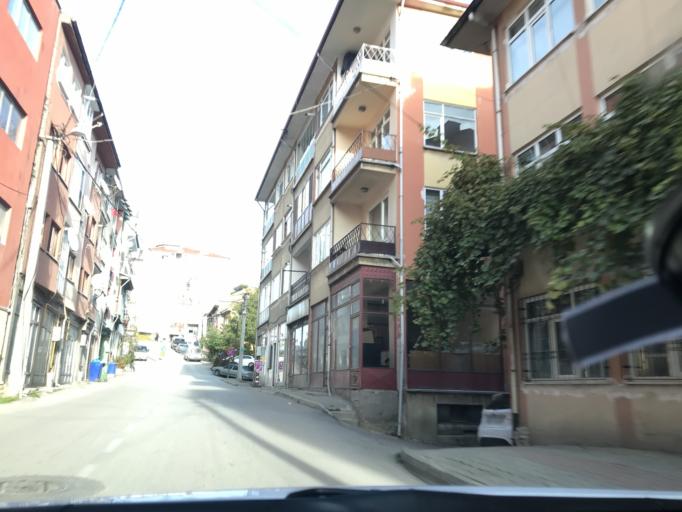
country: TR
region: Bolu
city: Bolu
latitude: 40.7331
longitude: 31.6128
